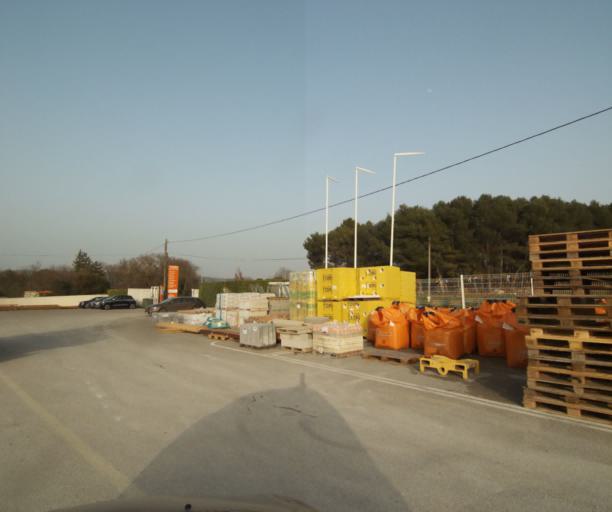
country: FR
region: Provence-Alpes-Cote d'Azur
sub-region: Departement des Bouches-du-Rhone
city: Eguilles
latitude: 43.5755
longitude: 5.3626
